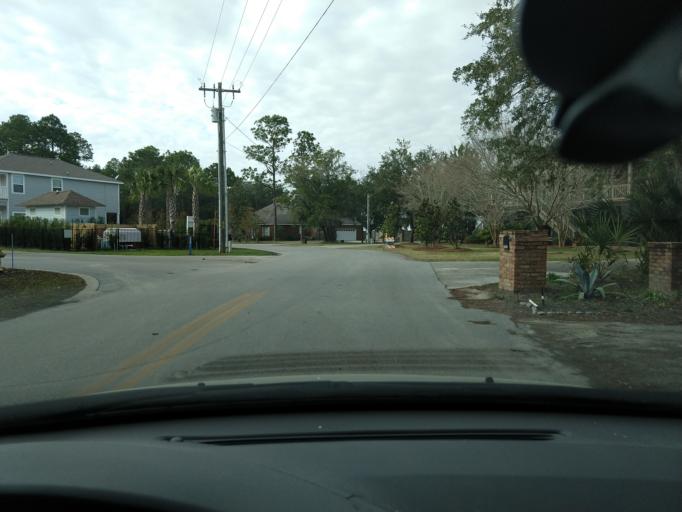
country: US
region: Florida
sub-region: Walton County
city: Seaside
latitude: 30.4008
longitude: -86.2071
